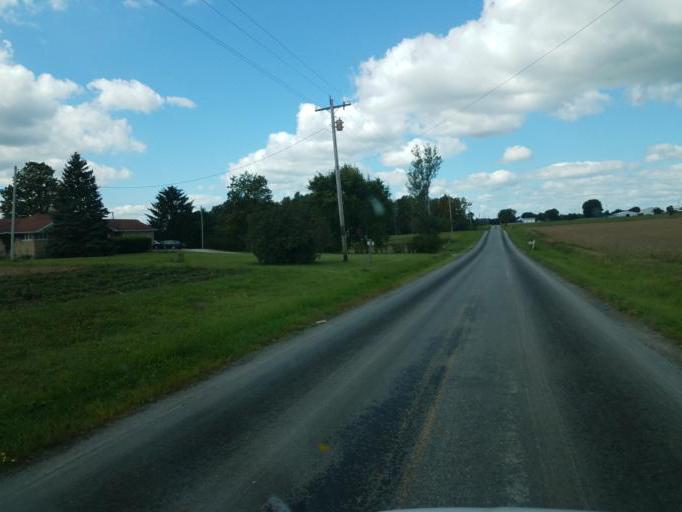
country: US
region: Ohio
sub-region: Wayne County
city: West Salem
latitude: 41.0425
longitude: -82.1172
